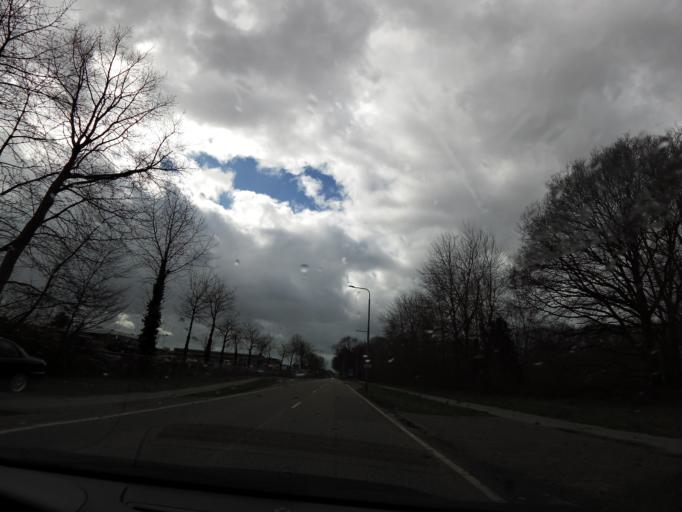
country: NL
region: Limburg
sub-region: Gemeente Venlo
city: Tegelen
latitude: 51.3214
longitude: 6.1178
